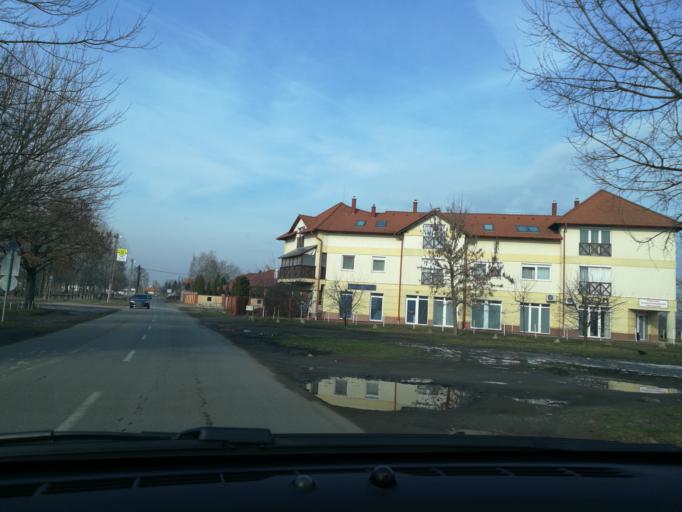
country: HU
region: Szabolcs-Szatmar-Bereg
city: Nyiregyhaza
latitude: 47.9622
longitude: 21.7356
